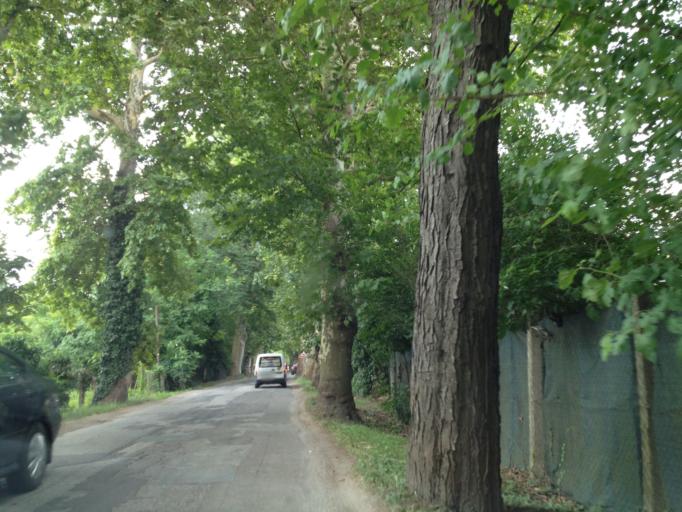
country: SK
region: Nitriansky
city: Komarno
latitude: 47.7554
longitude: 18.1115
